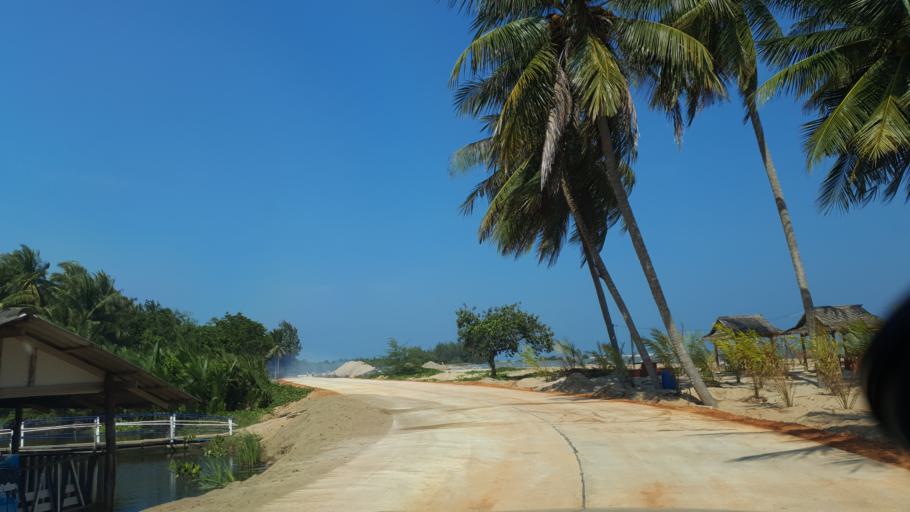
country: TH
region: Surat Thani
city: Tha Chana
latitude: 9.5884
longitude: 99.2078
